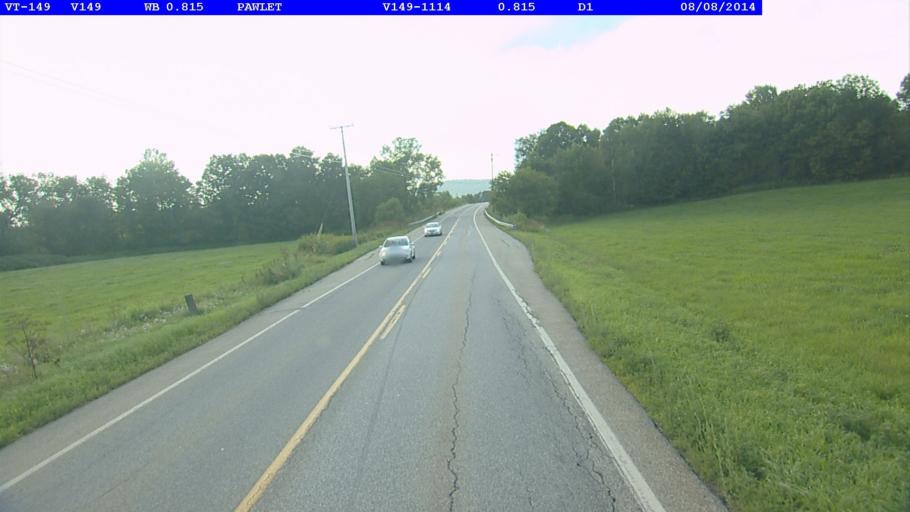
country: US
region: New York
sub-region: Washington County
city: Granville
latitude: 43.4028
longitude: -73.2355
